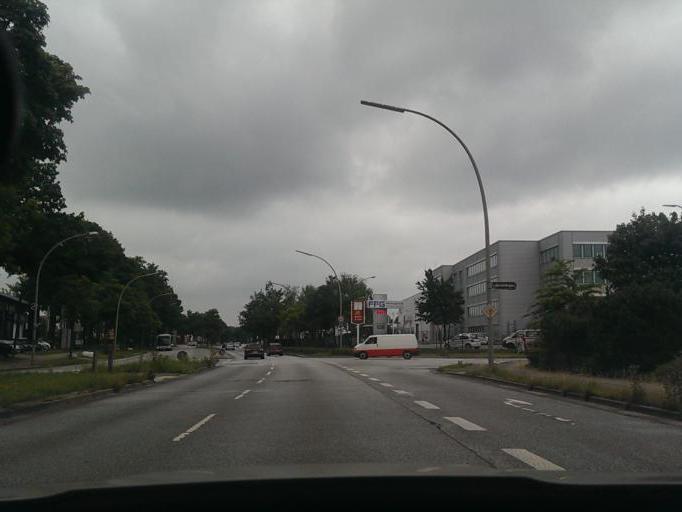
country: DE
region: Hamburg
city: Hummelsbuettel
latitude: 53.6494
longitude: 10.0333
